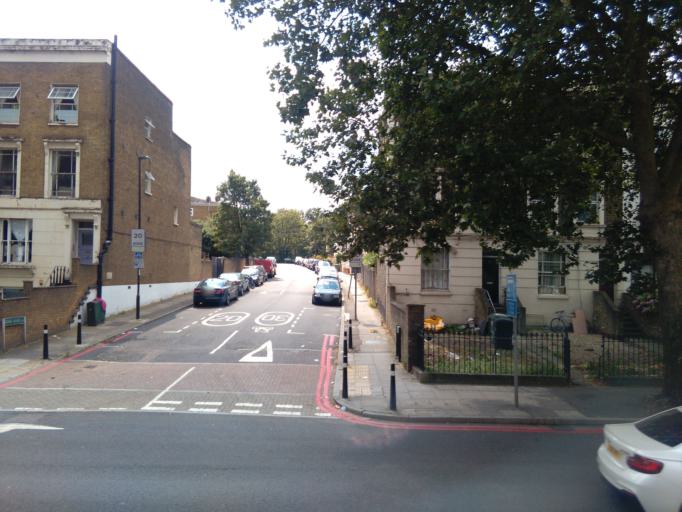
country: GB
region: England
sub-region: Greater London
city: Catford
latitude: 51.4756
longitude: -0.0306
